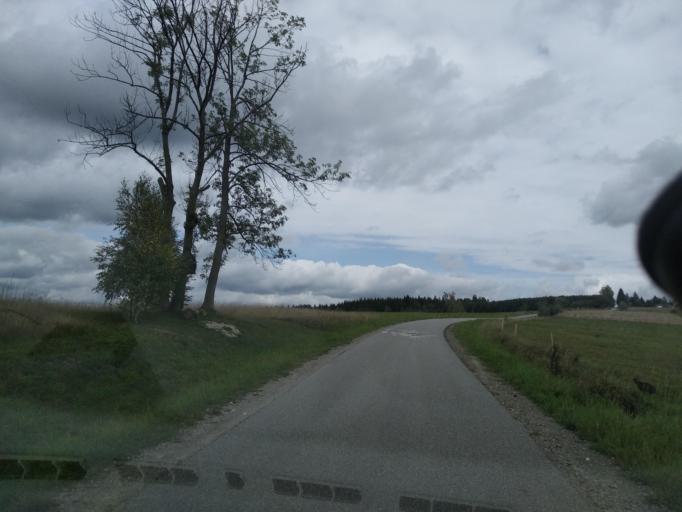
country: PL
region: Lesser Poland Voivodeship
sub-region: Powiat gorlicki
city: Uscie Gorlickie
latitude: 49.5344
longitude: 21.1768
